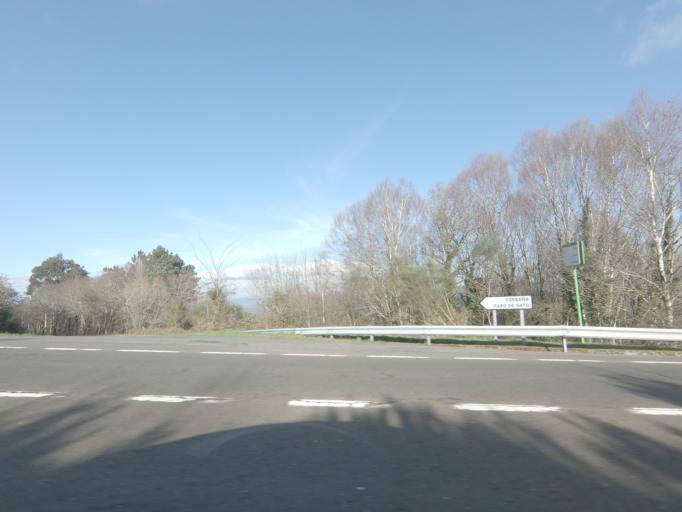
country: ES
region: Galicia
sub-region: Provincia de Pontevedra
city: Silleda
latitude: 42.7020
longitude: -8.3409
